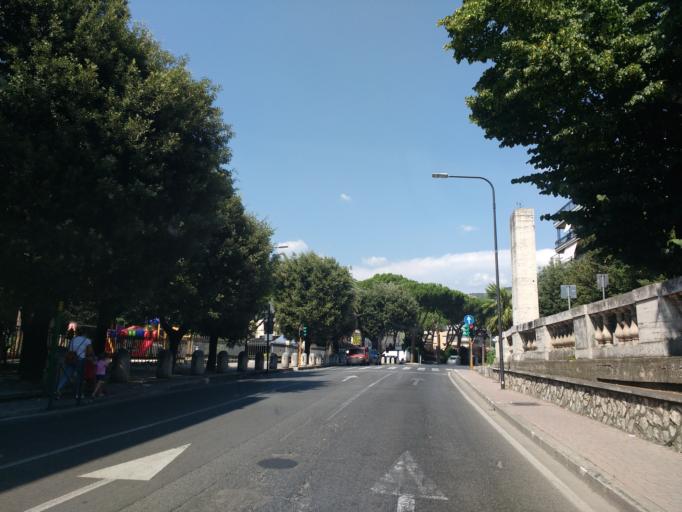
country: IT
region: Latium
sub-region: Citta metropolitana di Roma Capitale
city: Tivoli
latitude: 41.9598
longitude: 12.7950
